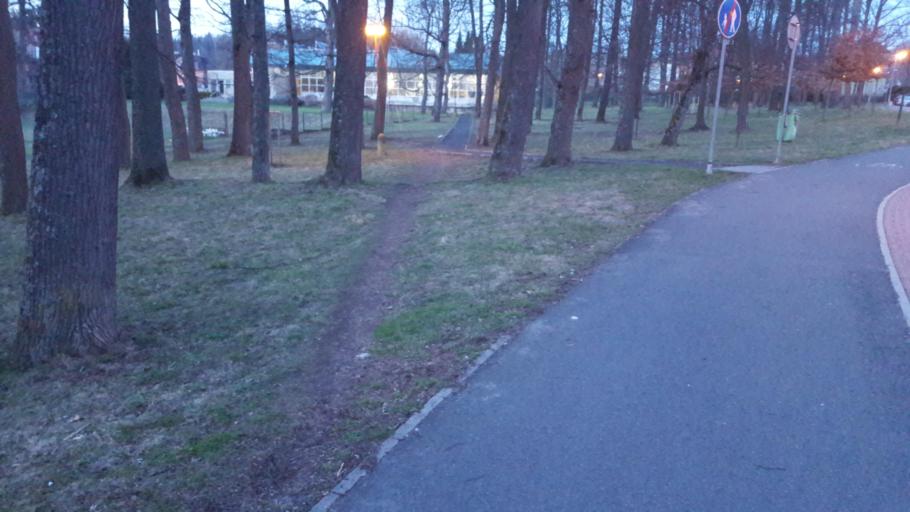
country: CZ
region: Karlovarsky
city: As
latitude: 50.2232
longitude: 12.1939
